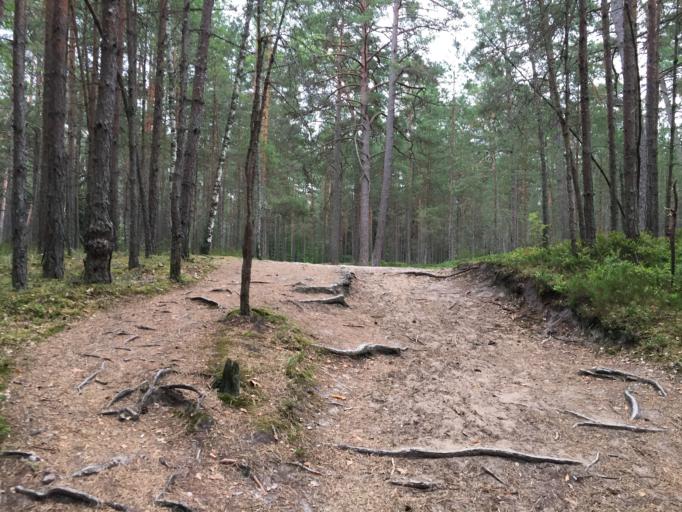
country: LV
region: Carnikava
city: Carnikava
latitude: 57.1208
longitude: 24.2190
